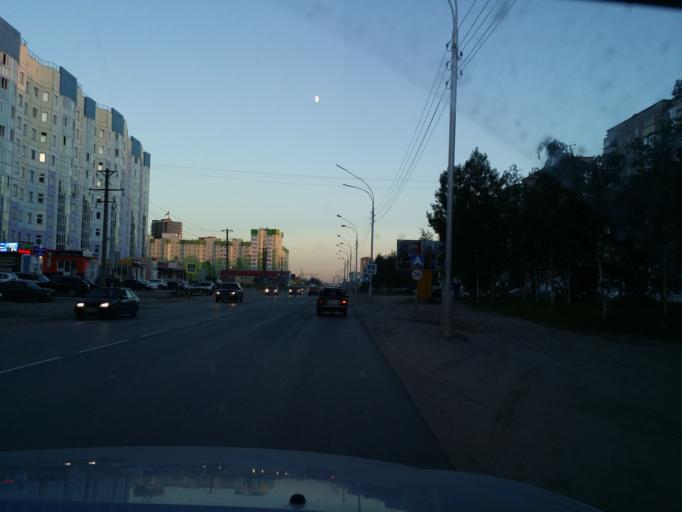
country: RU
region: Khanty-Mansiyskiy Avtonomnyy Okrug
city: Nizhnevartovsk
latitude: 60.9369
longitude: 76.6151
